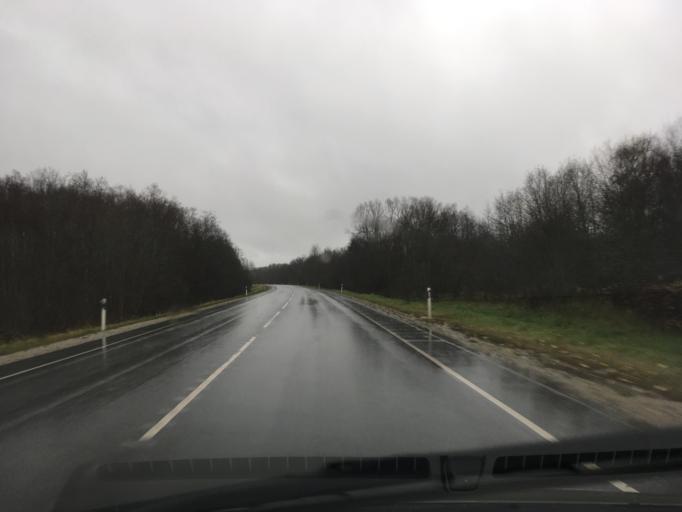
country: EE
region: Laeaene
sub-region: Lihula vald
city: Lihula
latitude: 58.8315
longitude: 24.0548
